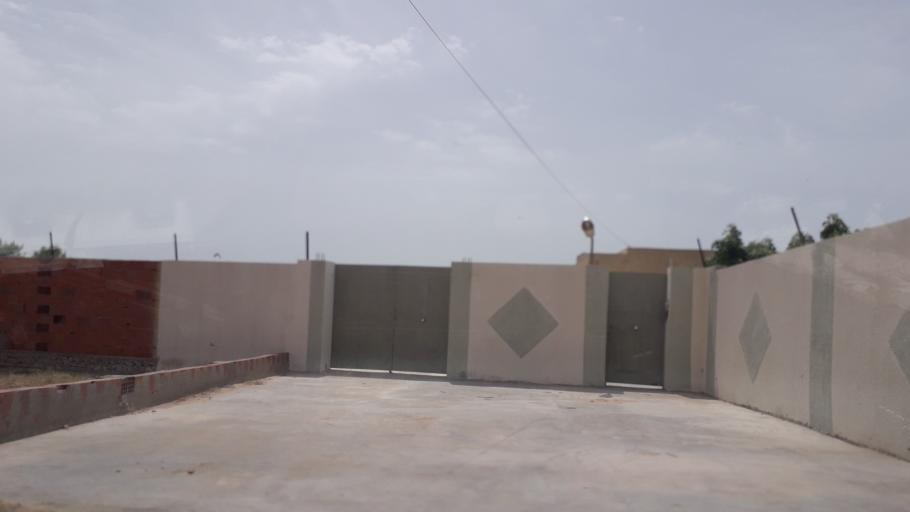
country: TN
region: Safaqis
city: Al Qarmadah
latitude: 34.8409
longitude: 10.7787
